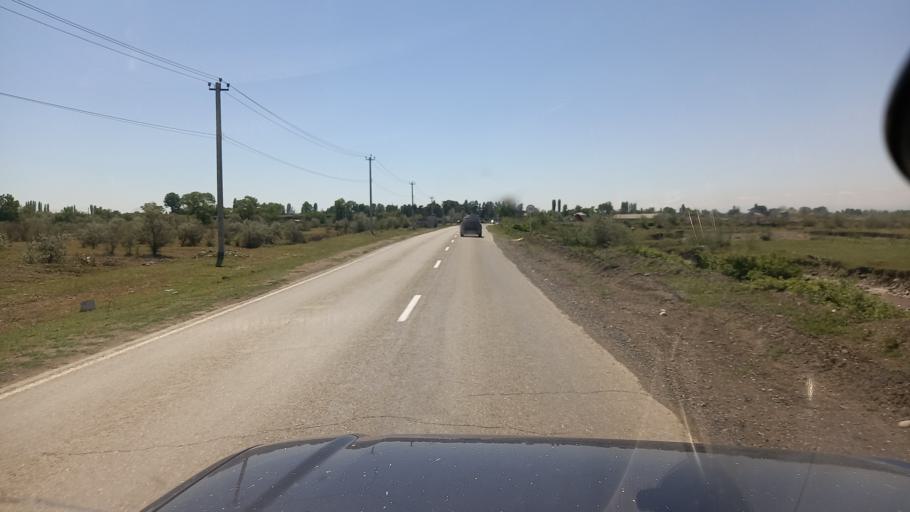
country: AZ
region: Qusar
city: Samur
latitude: 41.7319
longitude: 48.4534
